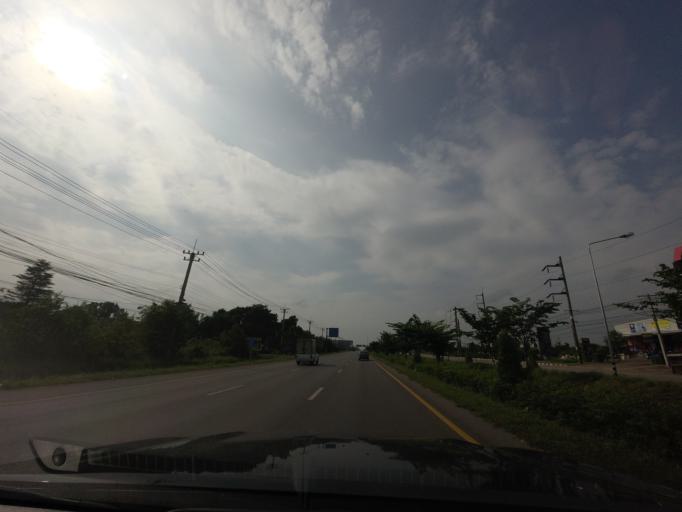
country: TH
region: Nong Khai
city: Nong Khai
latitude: 17.8185
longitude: 102.7580
